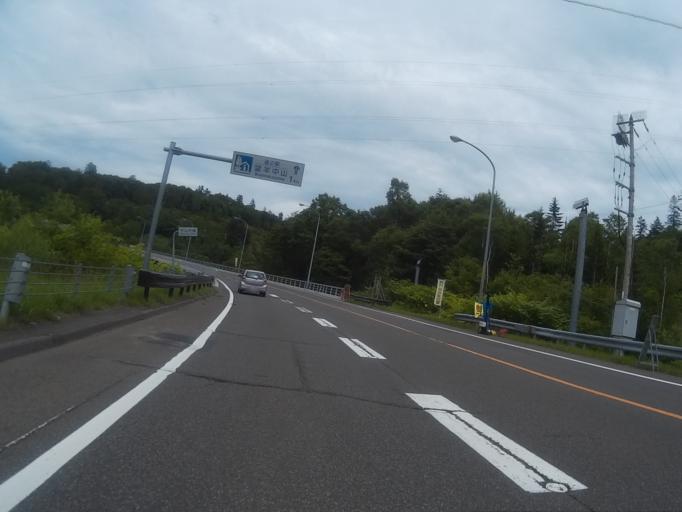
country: JP
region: Hokkaido
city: Sapporo
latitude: 42.8500
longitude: 141.0885
